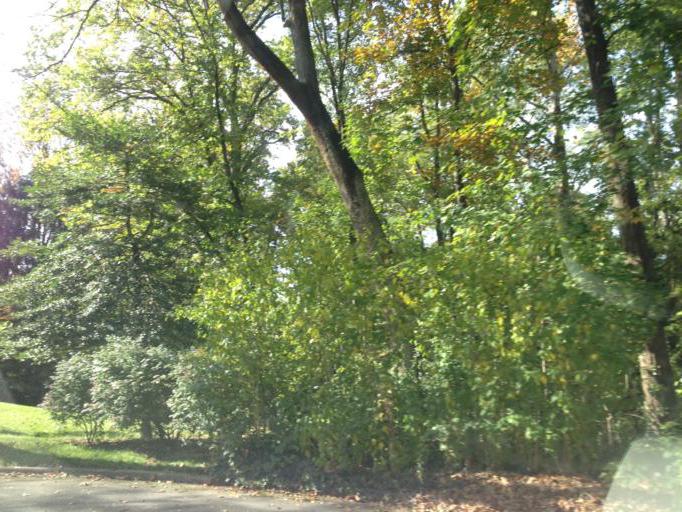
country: US
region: Maryland
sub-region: Howard County
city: Columbia
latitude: 39.2750
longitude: -76.8412
